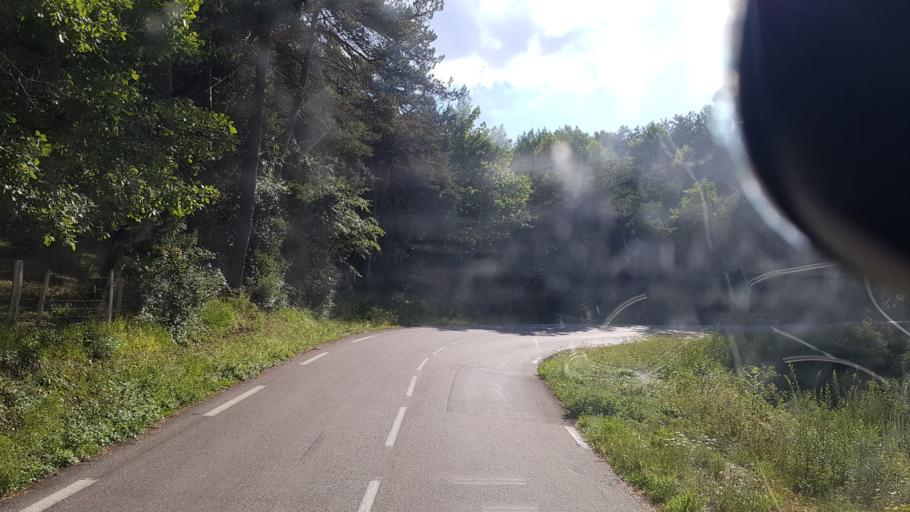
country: FR
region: Rhone-Alpes
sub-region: Departement de l'Isere
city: Mens
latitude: 44.8276
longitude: 5.6419
